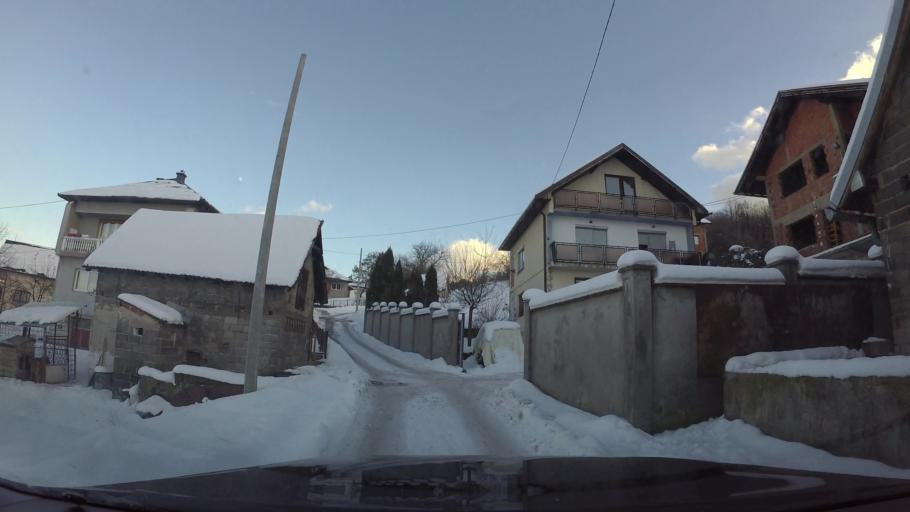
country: BA
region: Federation of Bosnia and Herzegovina
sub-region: Kanton Sarajevo
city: Sarajevo
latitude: 43.8080
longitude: 18.3525
